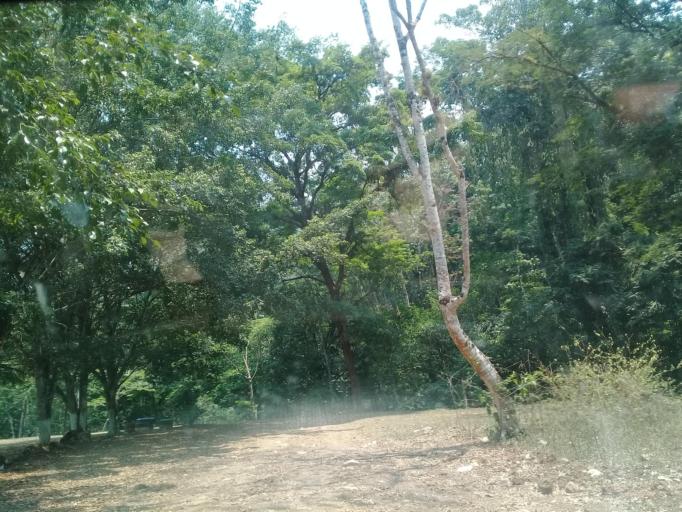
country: MX
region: Veracruz
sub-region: Tezonapa
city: Laguna Chica (Pueblo Nuevo)
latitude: 18.5673
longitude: -96.7300
